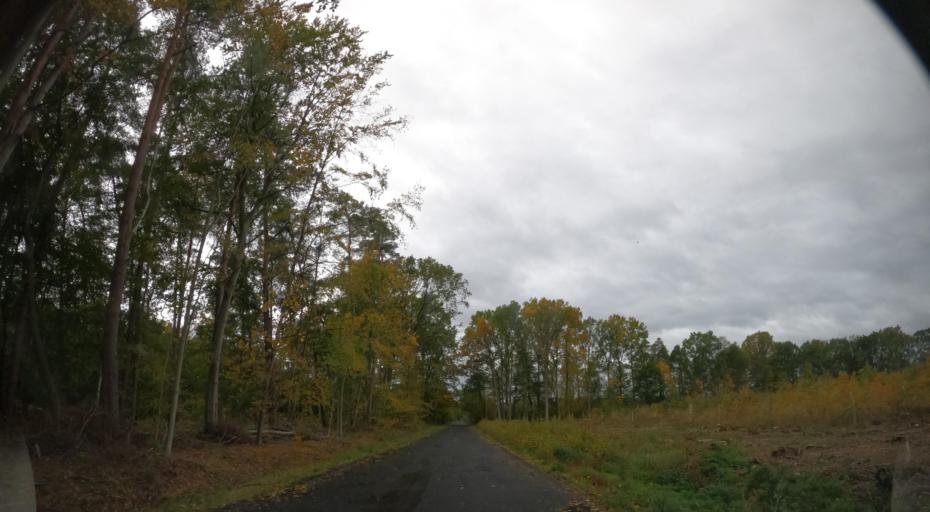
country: PL
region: West Pomeranian Voivodeship
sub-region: Powiat goleniowski
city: Stepnica
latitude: 53.6676
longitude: 14.6661
